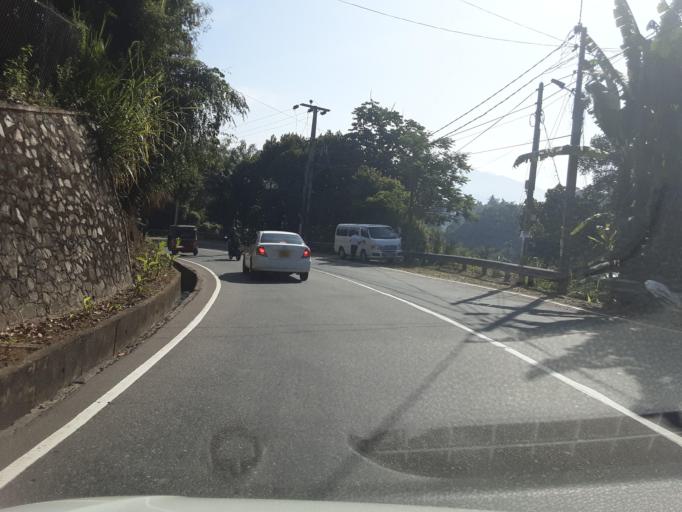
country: LK
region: Uva
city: Badulla
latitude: 6.9869
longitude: 81.0466
